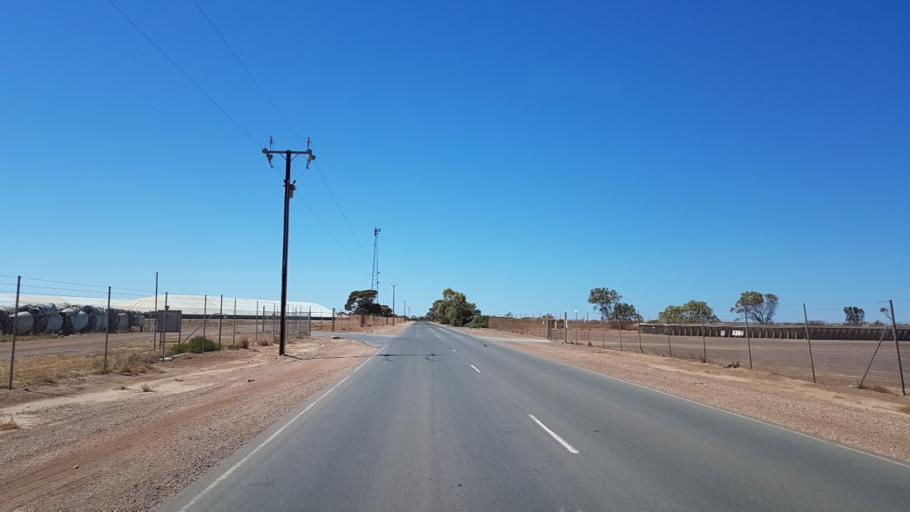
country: AU
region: South Australia
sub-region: Copper Coast
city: Wallaroo
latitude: -33.9398
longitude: 137.6126
